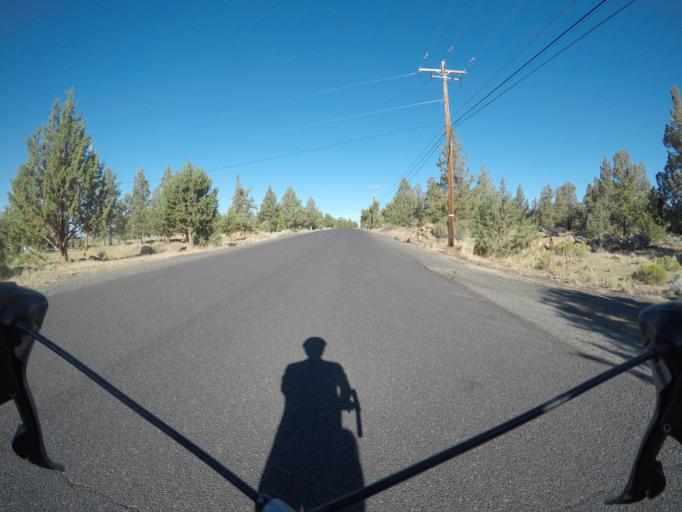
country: US
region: Oregon
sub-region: Deschutes County
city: Bend
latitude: 44.1729
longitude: -121.2709
